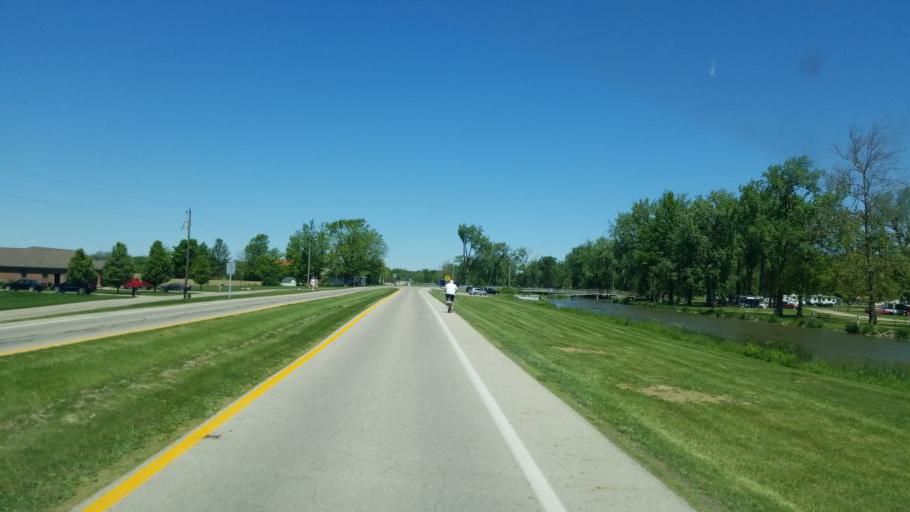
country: US
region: Ohio
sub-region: Shelby County
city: Fort Loramie
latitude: 40.3550
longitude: -84.3560
